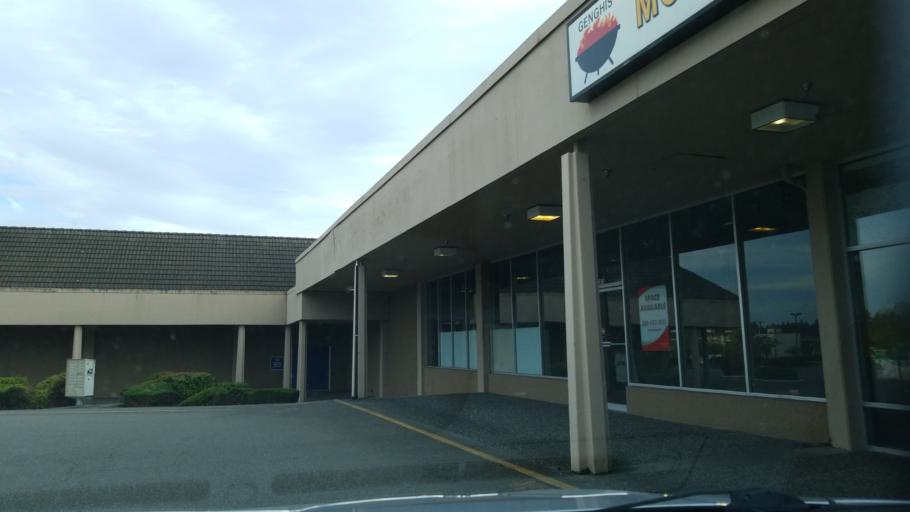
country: US
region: Washington
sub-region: Snohomish County
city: Alderwood Manor
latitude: 47.8200
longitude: -122.2947
